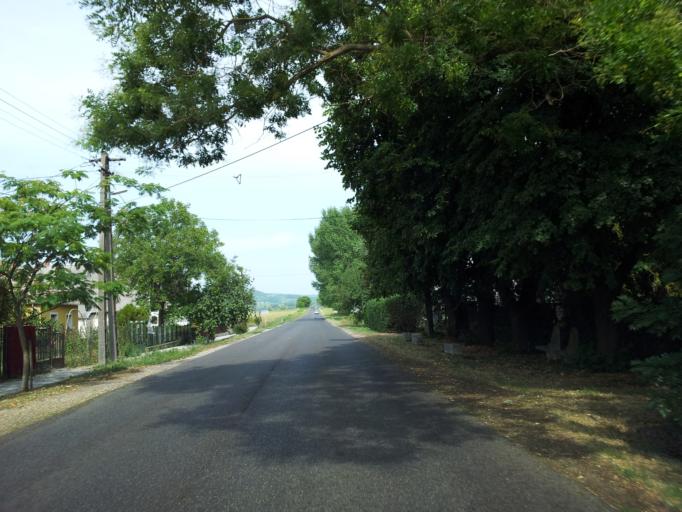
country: HU
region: Veszprem
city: Badacsonytomaj
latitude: 46.8387
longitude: 17.4873
